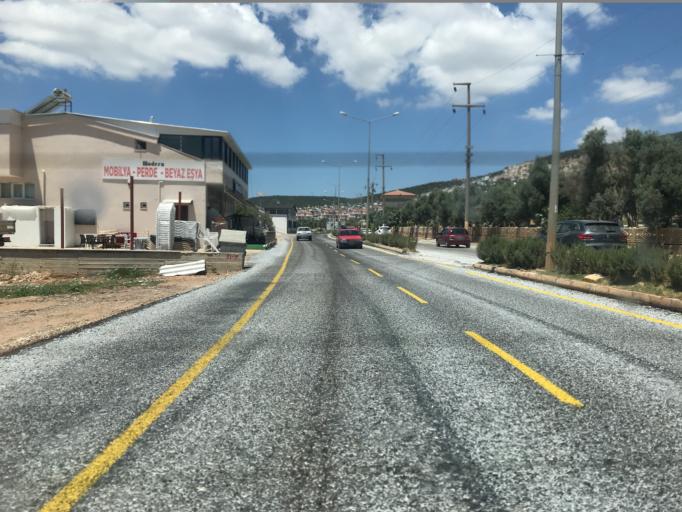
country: TR
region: Aydin
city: Sarikemer
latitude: 37.4148
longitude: 27.4203
